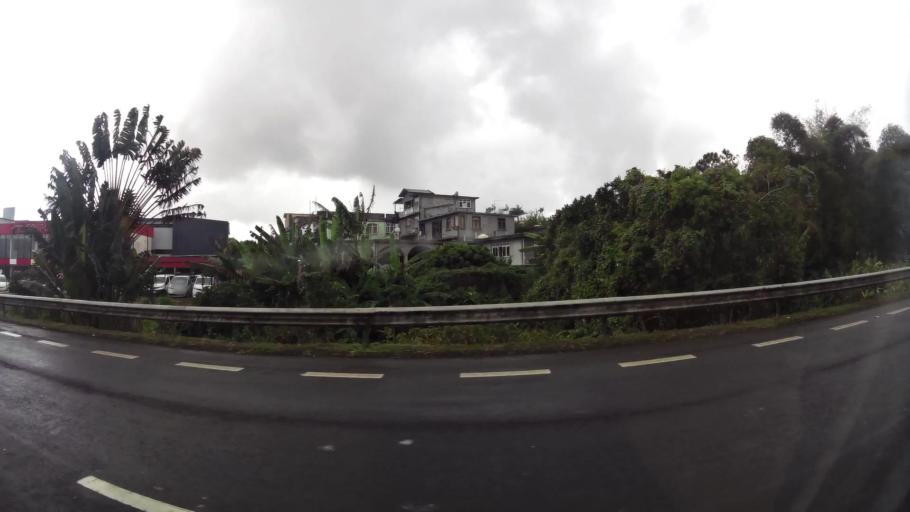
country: MU
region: Plaines Wilhems
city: Curepipe
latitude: -20.2895
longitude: 57.5261
